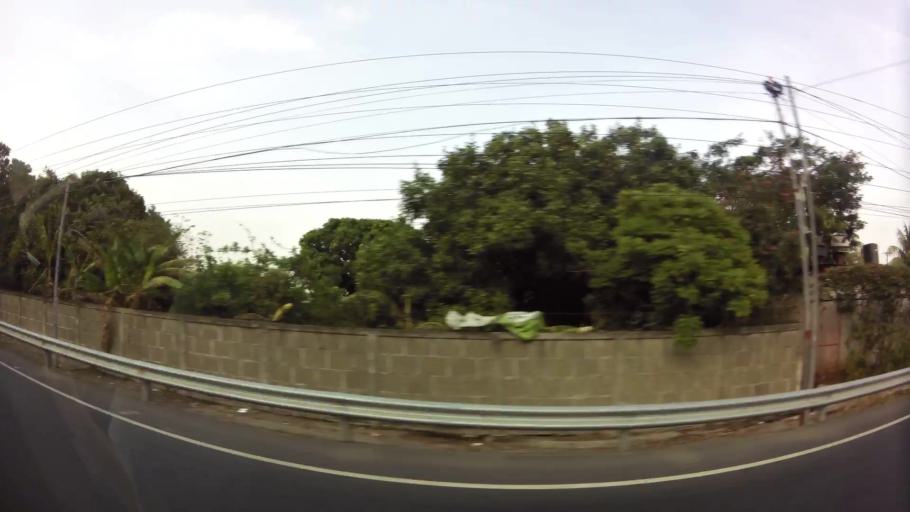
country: NI
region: Managua
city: Ciudad Sandino
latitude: 12.1463
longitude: -86.3355
